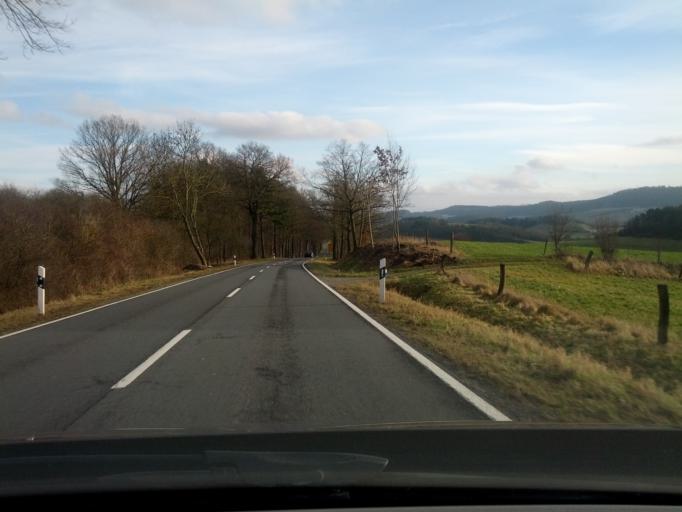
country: DE
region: Hesse
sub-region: Regierungsbezirk Kassel
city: Weissenborn
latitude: 51.0832
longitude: 10.1391
